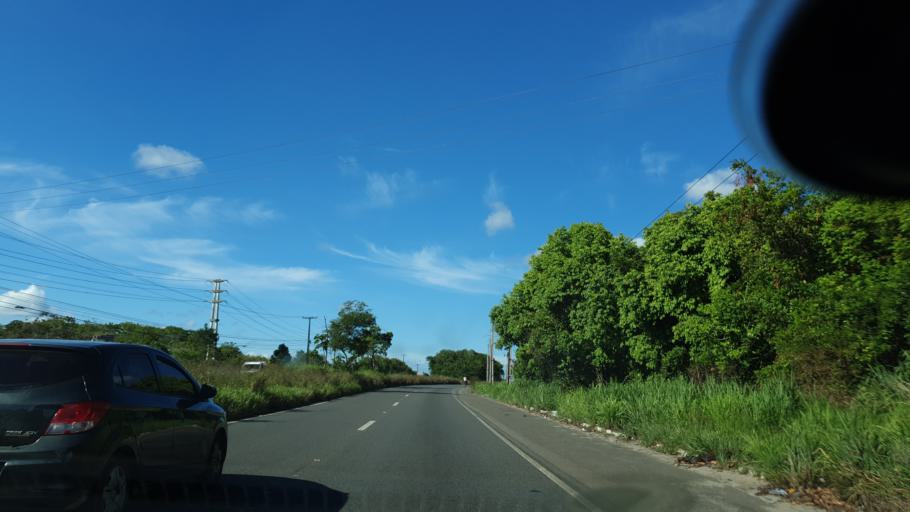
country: BR
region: Bahia
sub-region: Camacari
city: Camacari
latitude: -12.6797
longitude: -38.3021
